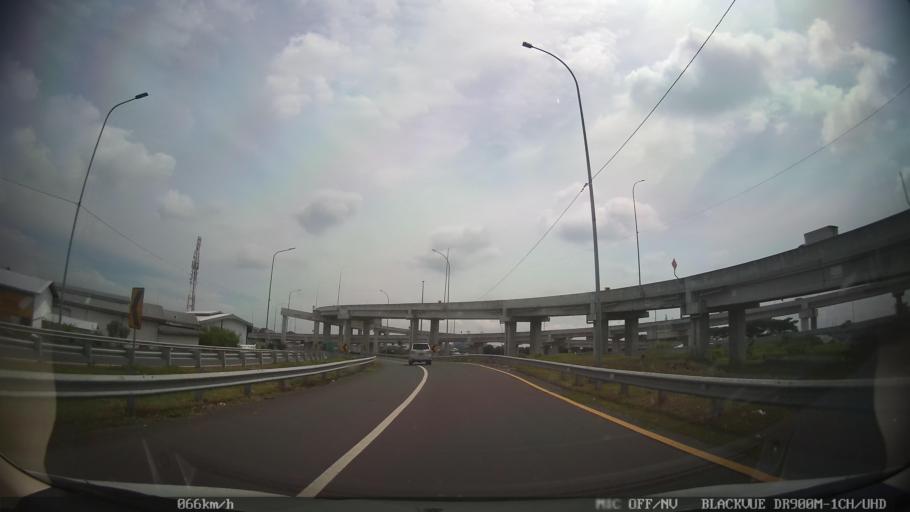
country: ID
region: North Sumatra
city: Medan
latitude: 3.6502
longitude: 98.6814
